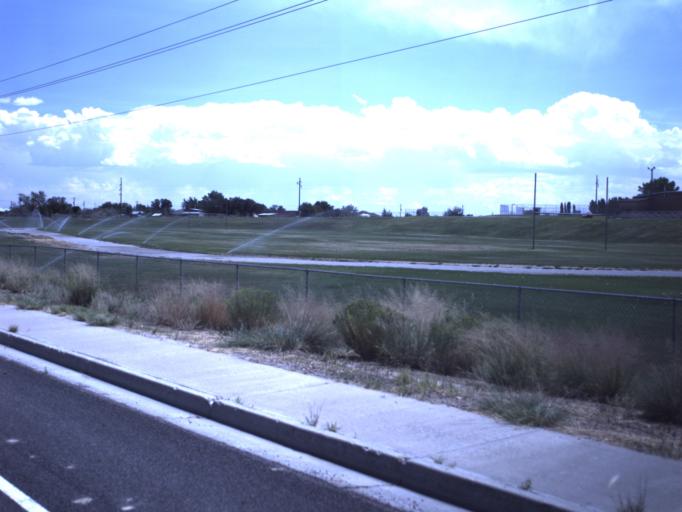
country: US
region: Utah
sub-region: Emery County
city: Huntington
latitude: 39.3380
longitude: -110.9729
